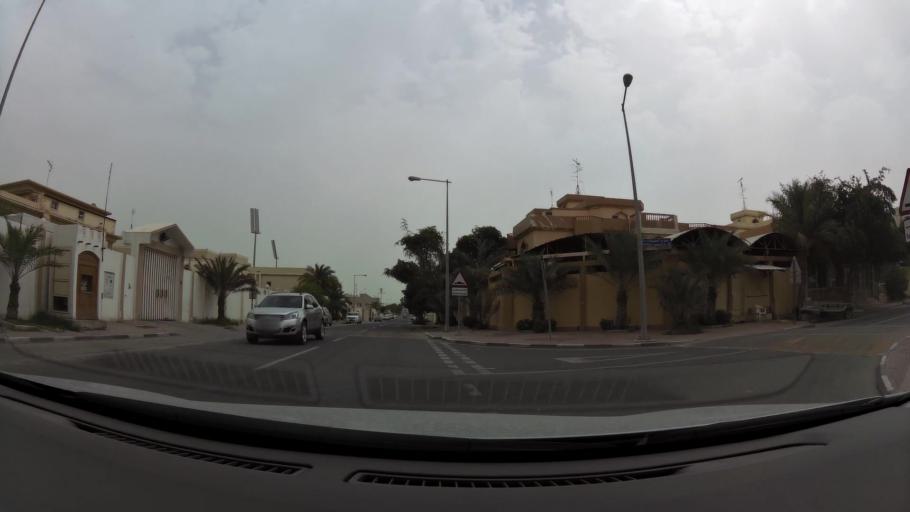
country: QA
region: Baladiyat ad Dawhah
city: Doha
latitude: 25.2569
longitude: 51.5173
